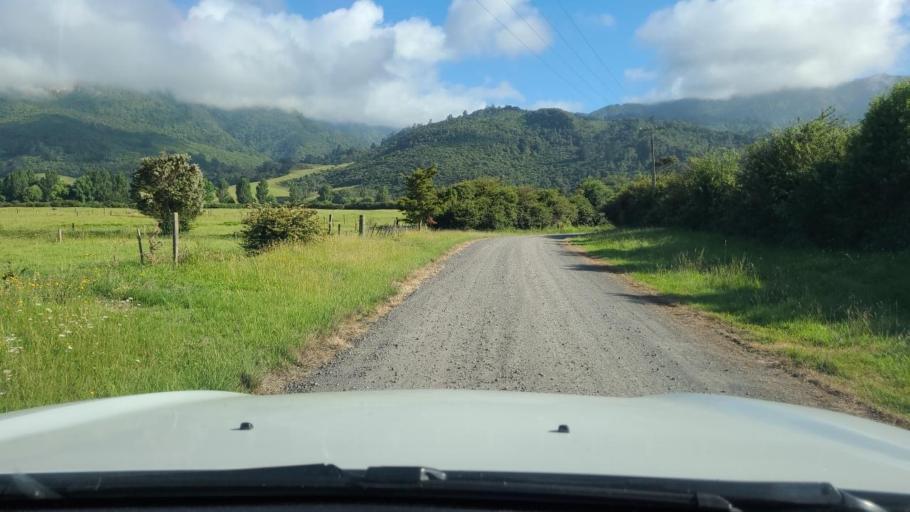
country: NZ
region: Bay of Plenty
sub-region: Western Bay of Plenty District
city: Katikati
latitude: -37.5738
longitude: 175.7622
